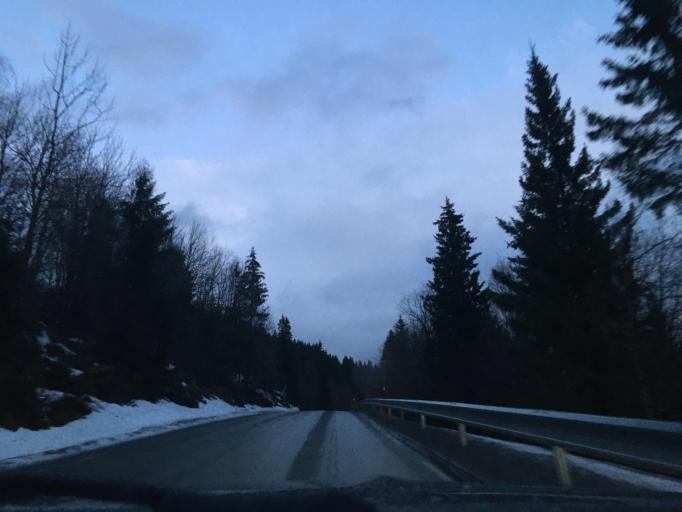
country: NO
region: Nordland
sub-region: Rana
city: Hauknes
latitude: 66.3047
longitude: 13.9556
